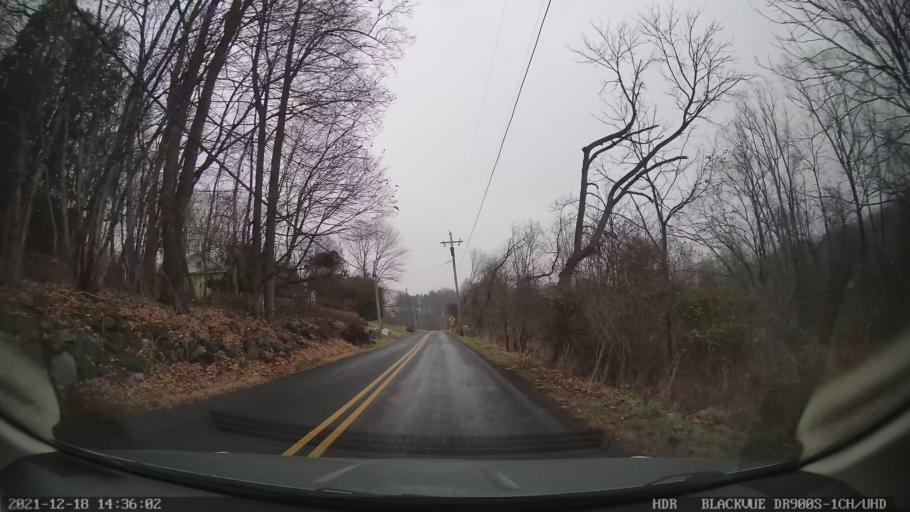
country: US
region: Pennsylvania
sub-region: Berks County
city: New Berlinville
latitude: 40.3861
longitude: -75.6550
